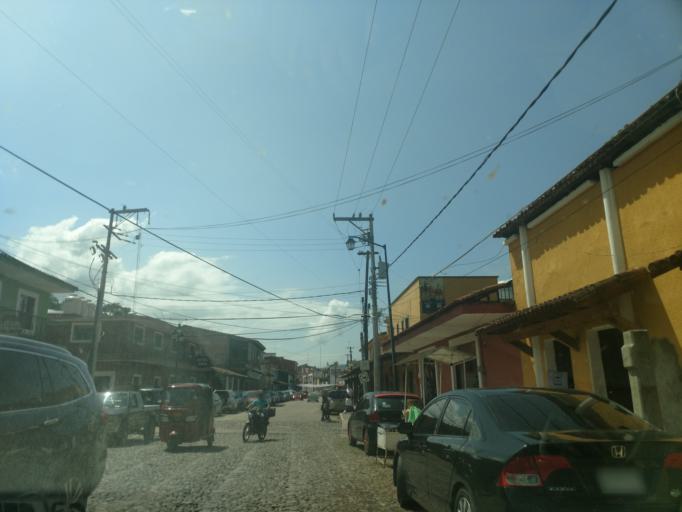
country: MX
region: Jalisco
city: Talpa de Allende
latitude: 20.3845
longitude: -104.8236
